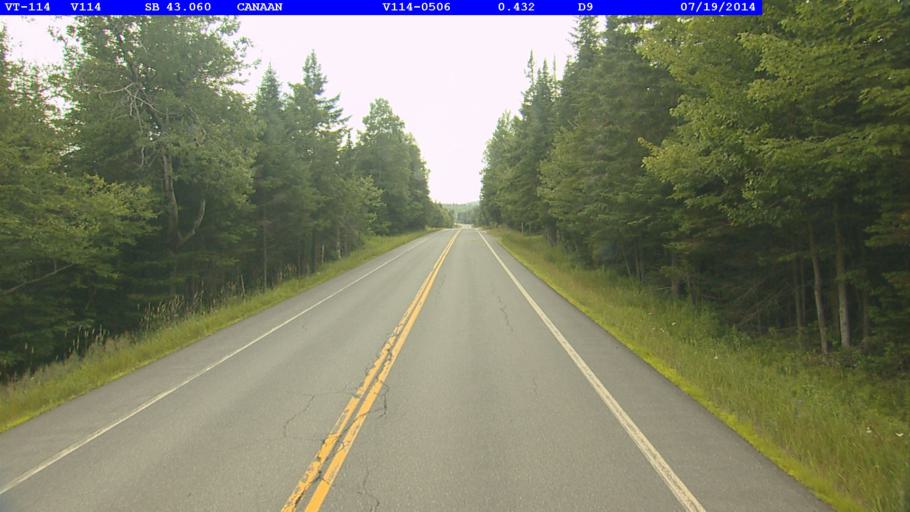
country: CA
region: Quebec
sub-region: Estrie
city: Coaticook
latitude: 45.0058
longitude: -71.6848
